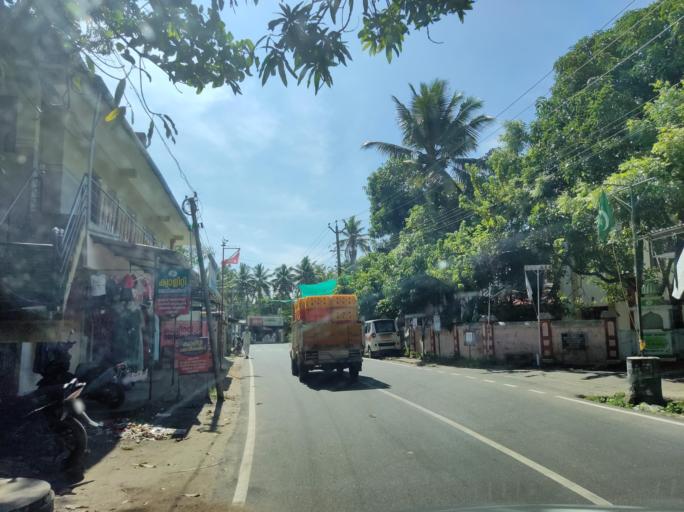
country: IN
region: Kerala
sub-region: Alappuzha
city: Kayankulam
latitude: 9.2845
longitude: 76.3977
